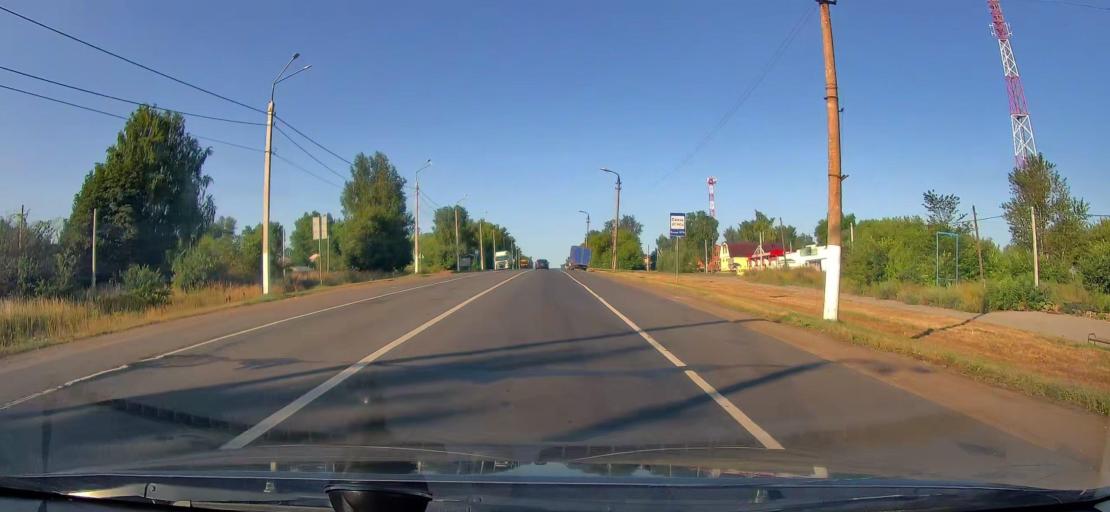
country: RU
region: Tula
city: Plavsk
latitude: 53.6963
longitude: 37.2801
